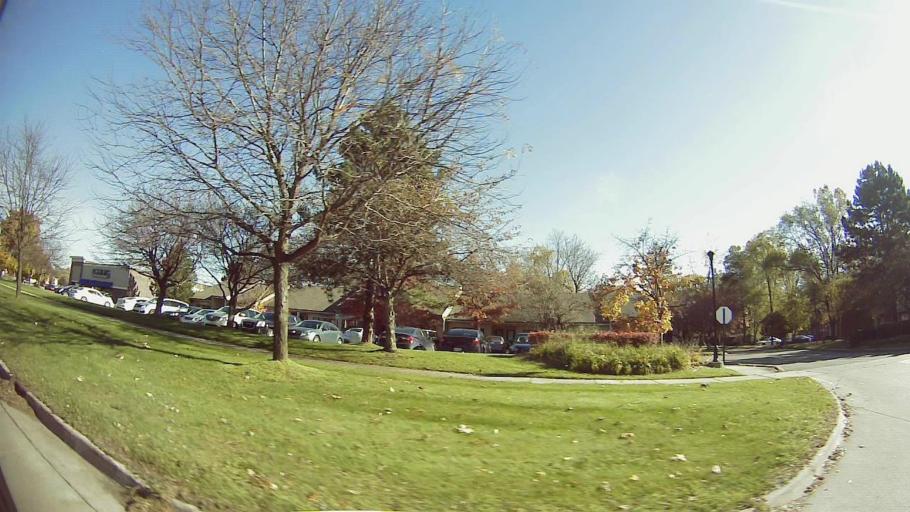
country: US
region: Michigan
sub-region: Oakland County
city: Farmington
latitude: 42.4530
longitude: -83.3756
